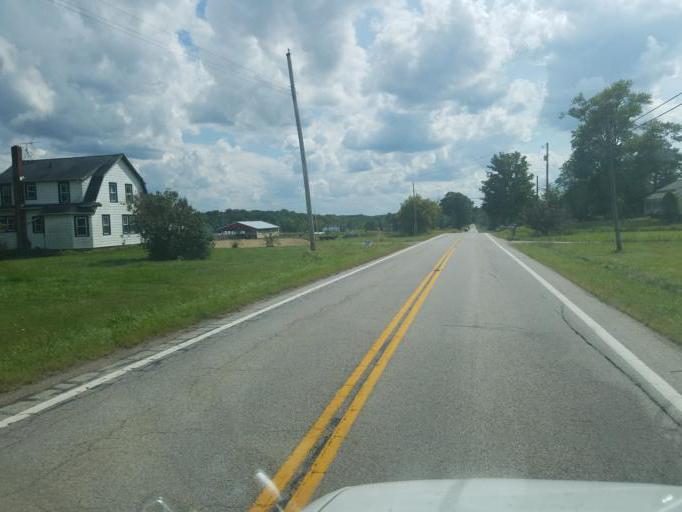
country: US
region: Ohio
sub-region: Portage County
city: Hiram
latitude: 41.3520
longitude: -81.1432
